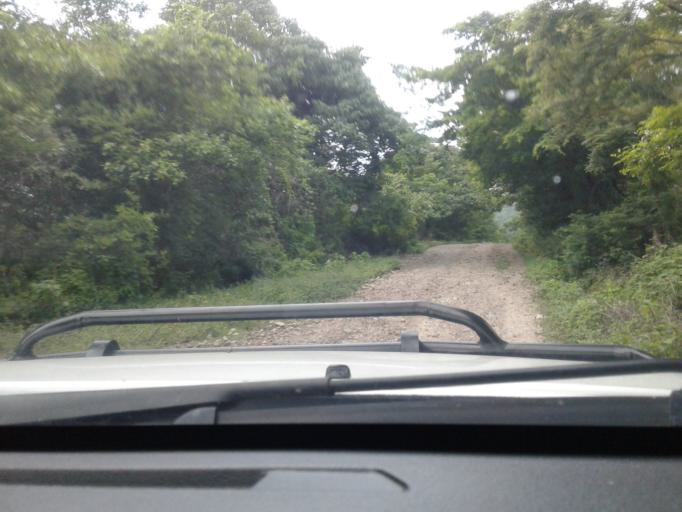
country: NI
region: Leon
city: Santa Rosa del Penon
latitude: 12.9041
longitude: -86.2174
